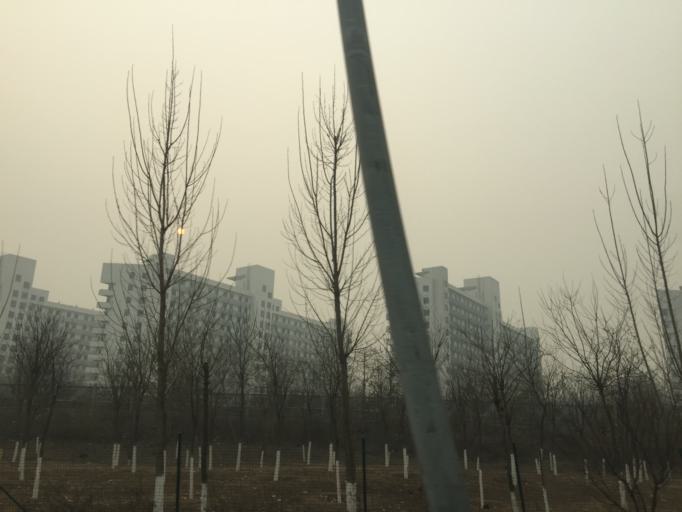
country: CN
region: Beijing
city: Qinghe
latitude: 40.0105
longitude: 116.3285
